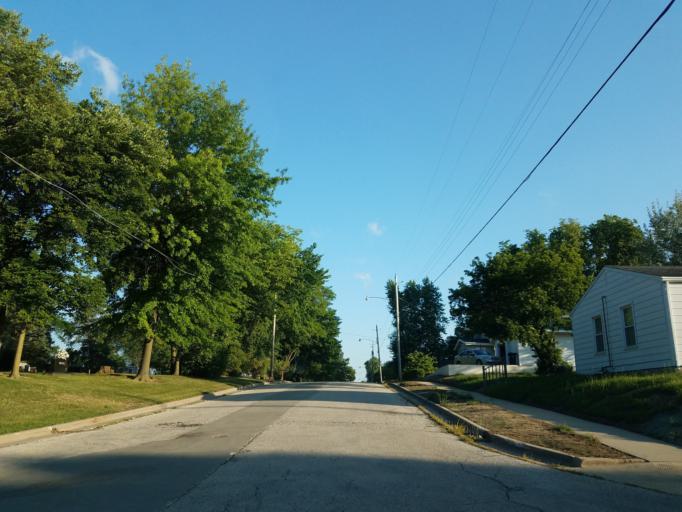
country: US
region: Illinois
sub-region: McLean County
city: Bloomington
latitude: 40.4697
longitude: -89.0098
